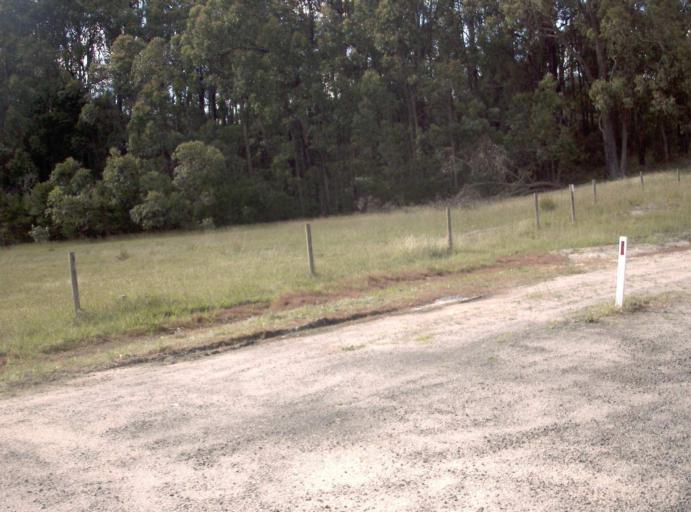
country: AU
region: Victoria
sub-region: Latrobe
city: Moe
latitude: -38.1843
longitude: 146.3278
